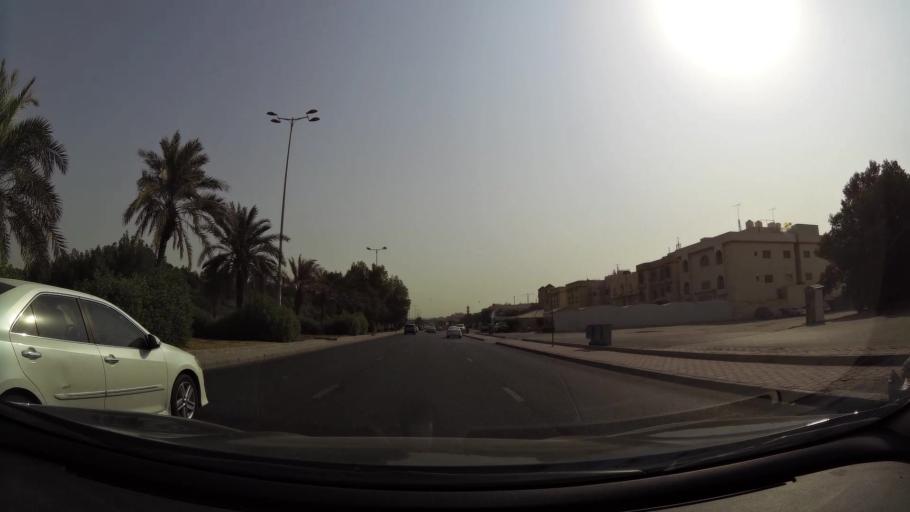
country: KW
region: Al Asimah
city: Ar Rabiyah
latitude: 29.2744
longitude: 47.8762
